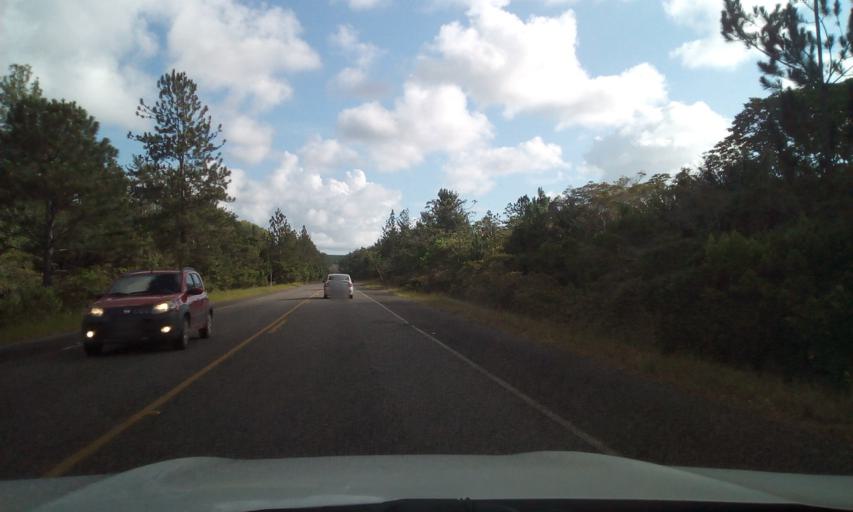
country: BR
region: Bahia
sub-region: Entre Rios
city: Entre Rios
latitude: -12.1505
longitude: -37.7996
